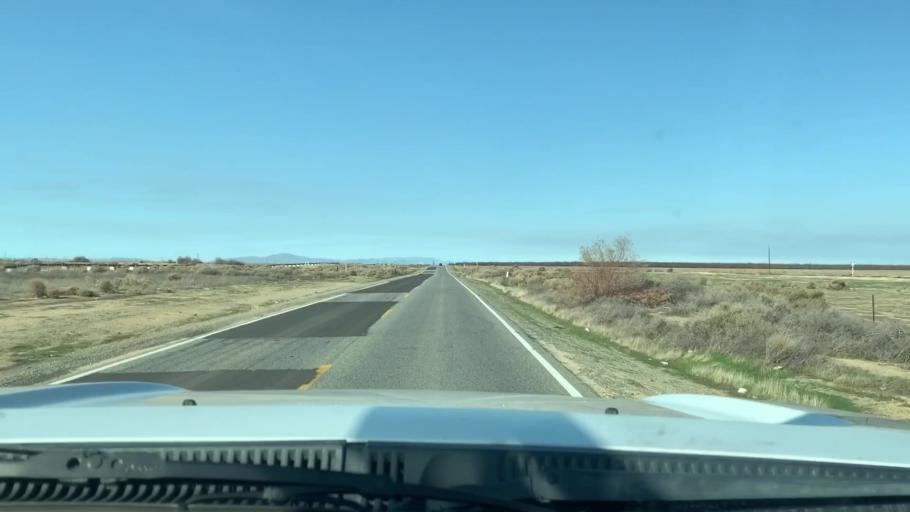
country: US
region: California
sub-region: Kern County
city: Lost Hills
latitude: 35.5502
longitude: -119.7880
